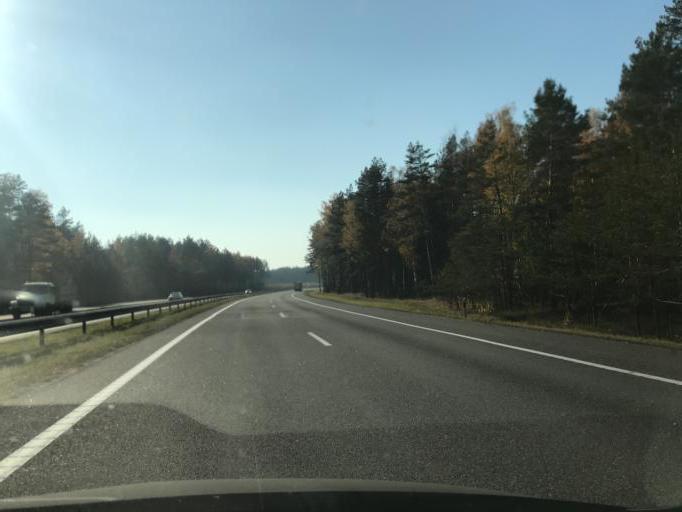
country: BY
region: Minsk
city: Enyerhyetykaw
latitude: 53.5536
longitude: 26.9656
